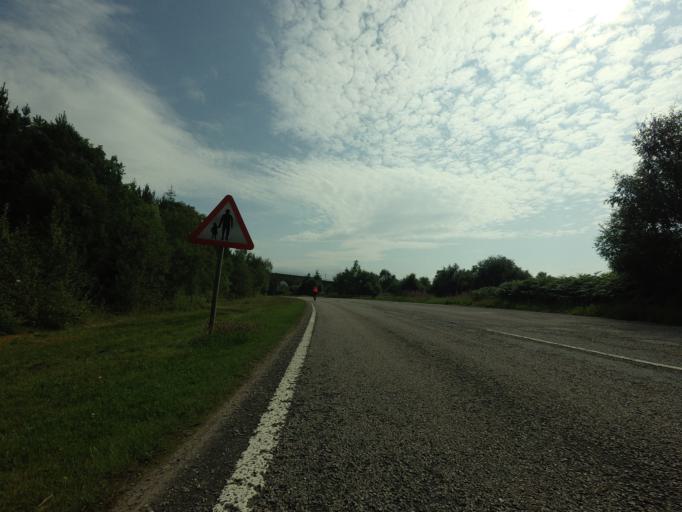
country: GB
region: Scotland
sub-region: Highland
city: Evanton
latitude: 57.9255
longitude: -4.4009
